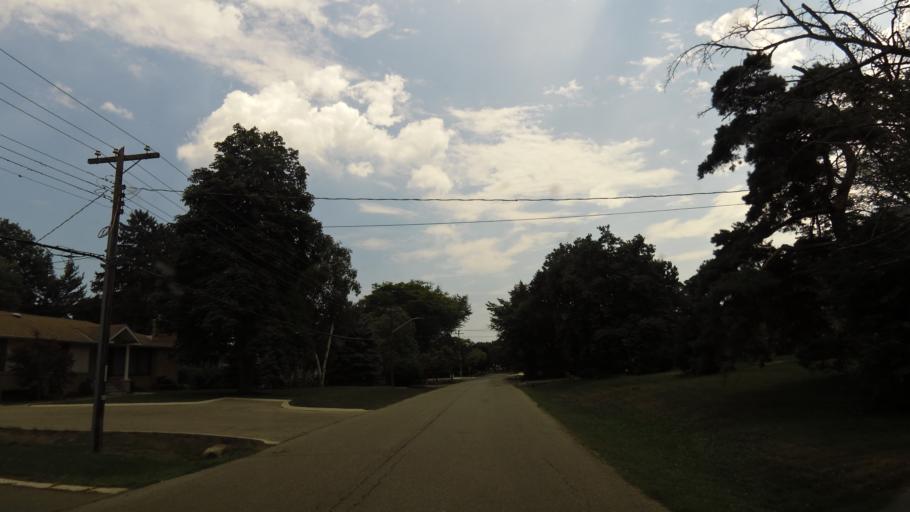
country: CA
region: Ontario
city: Mississauga
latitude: 43.5676
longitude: -79.5863
